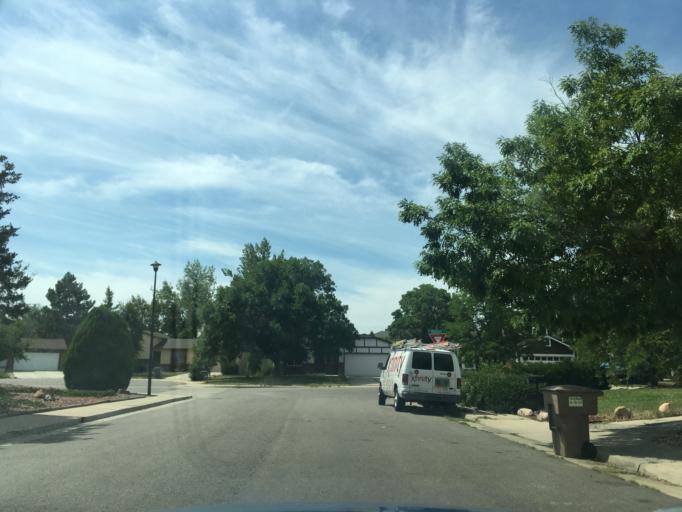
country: US
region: Colorado
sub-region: Adams County
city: Aurora
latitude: 39.7161
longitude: -104.8587
